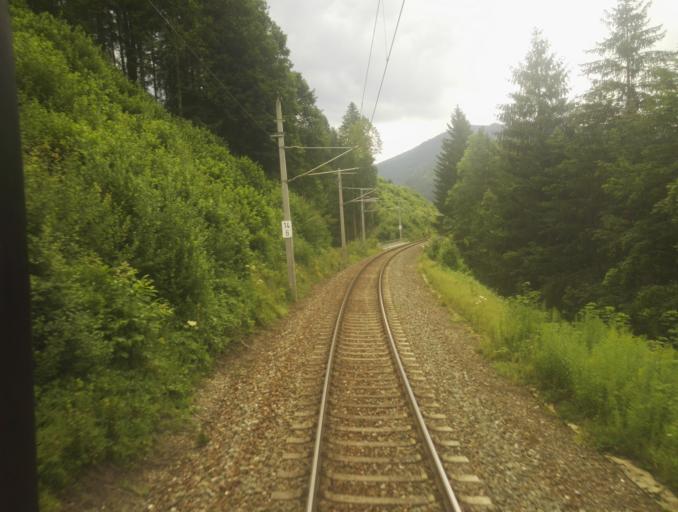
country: AT
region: Salzburg
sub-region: Politischer Bezirk Sankt Johann im Pongau
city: Eben im Pongau
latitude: 47.4202
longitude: 13.3750
